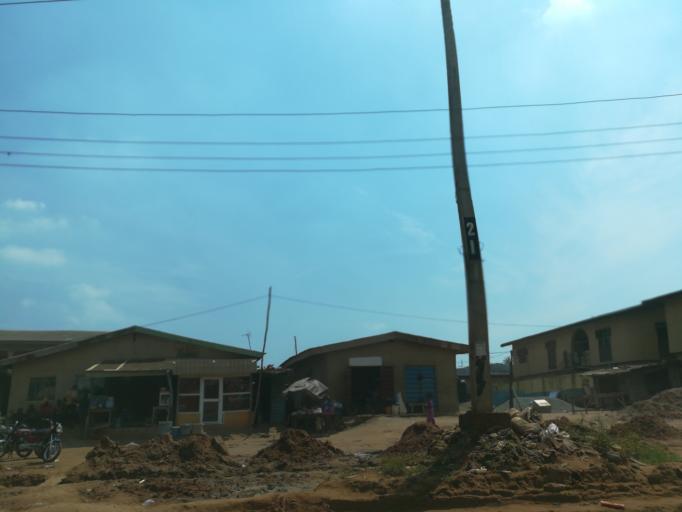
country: NG
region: Lagos
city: Ikorodu
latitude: 6.6477
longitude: 3.4781
